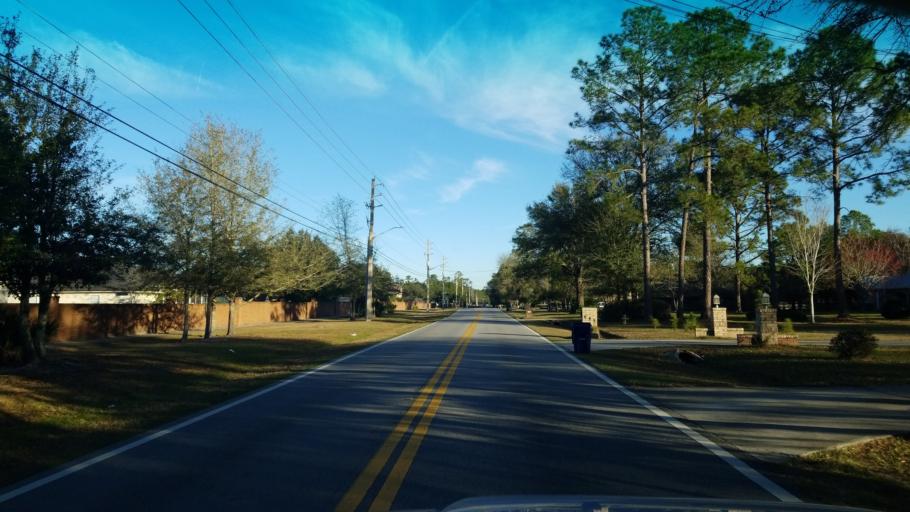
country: US
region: Florida
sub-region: Duval County
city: Baldwin
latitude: 30.3258
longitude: -81.8486
